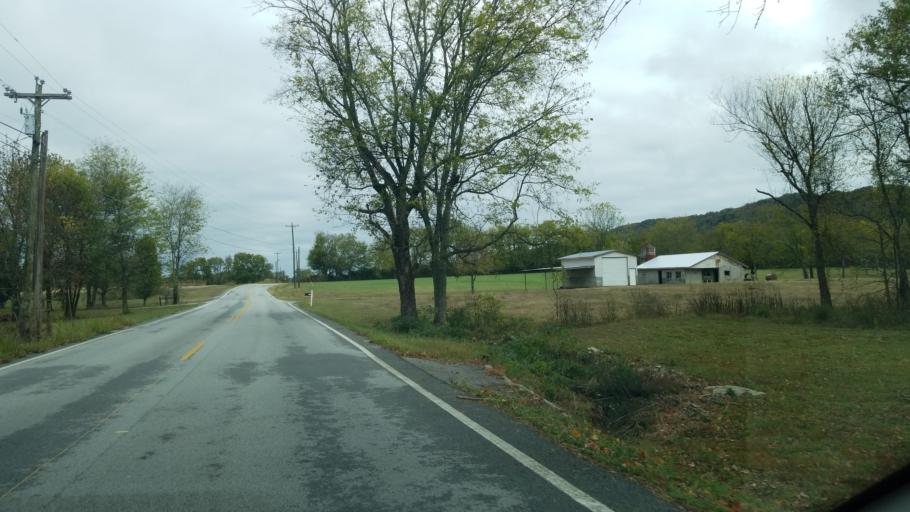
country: US
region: Tennessee
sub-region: Hamilton County
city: Lakesite
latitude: 35.1881
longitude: -85.0214
